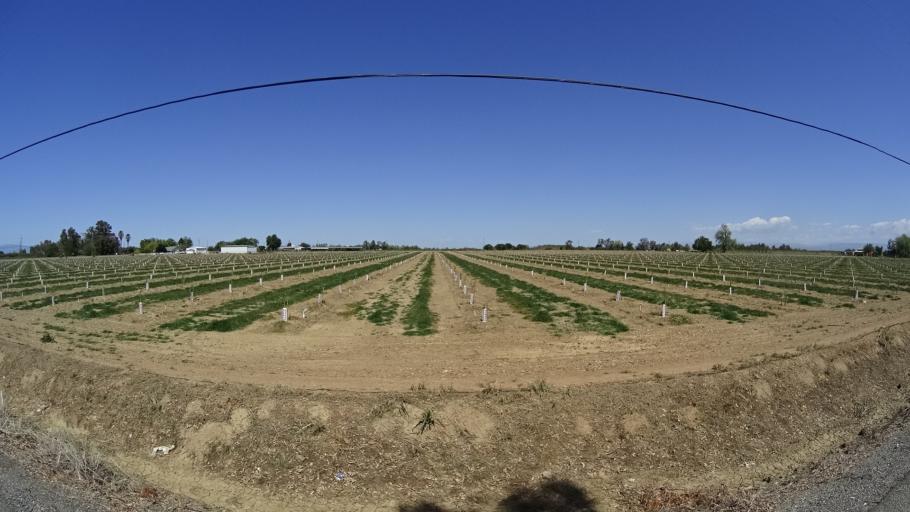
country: US
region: California
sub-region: Glenn County
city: Orland
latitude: 39.7867
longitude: -122.1947
